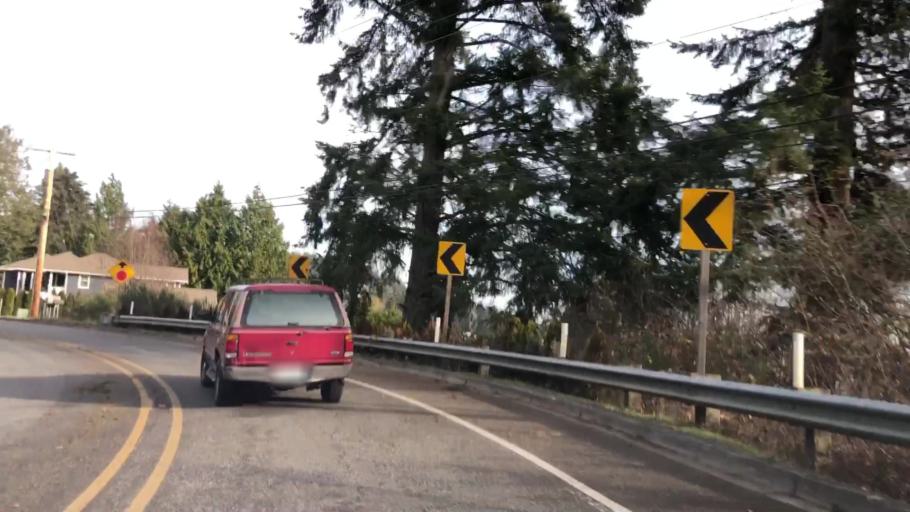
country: US
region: Washington
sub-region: Kitsap County
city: Kingston
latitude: 47.7950
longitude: -122.5092
